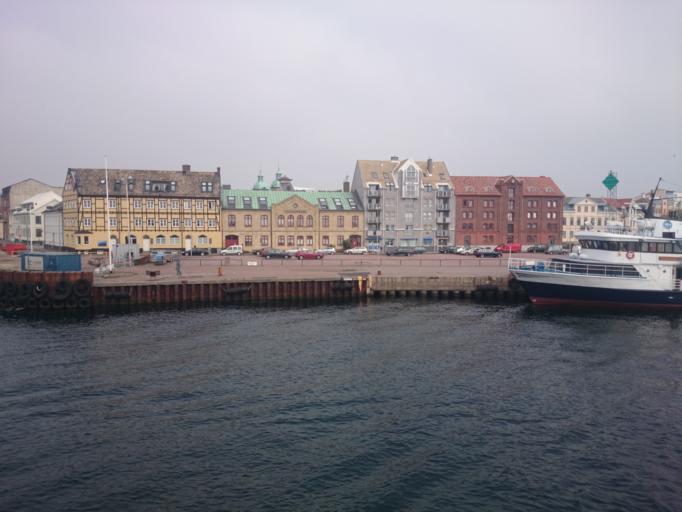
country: SE
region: Skane
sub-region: Landskrona
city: Landskrona
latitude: 55.8663
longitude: 12.8231
